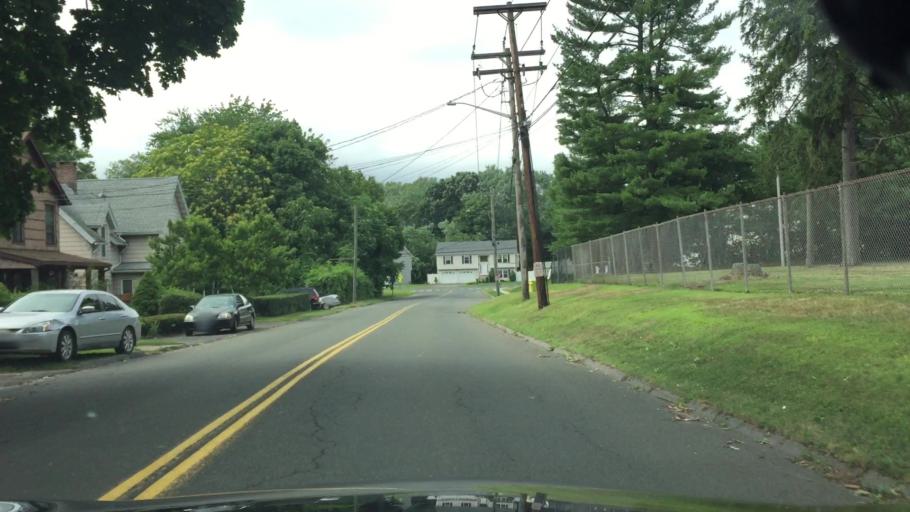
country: US
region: Connecticut
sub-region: New Haven County
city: City of Milford (balance)
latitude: 41.2224
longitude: -73.0669
